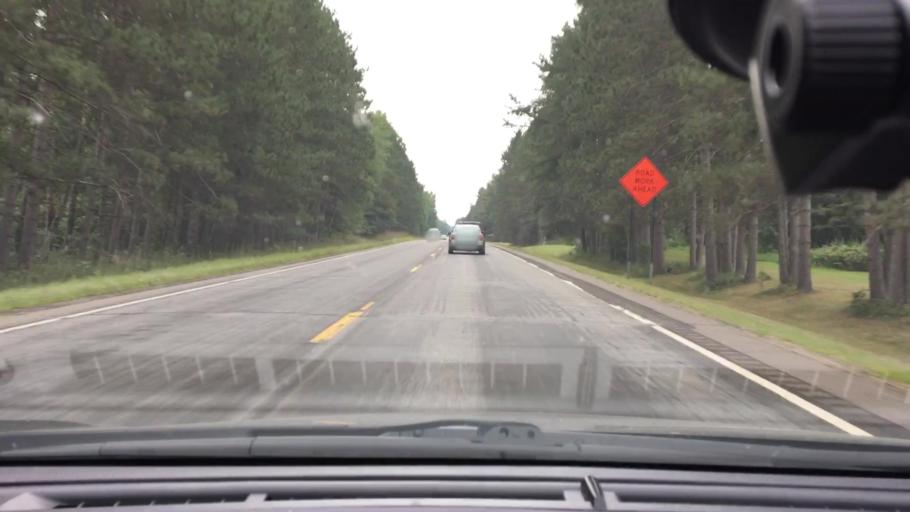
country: US
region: Minnesota
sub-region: Crow Wing County
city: Cross Lake
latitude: 46.7520
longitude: -93.9671
